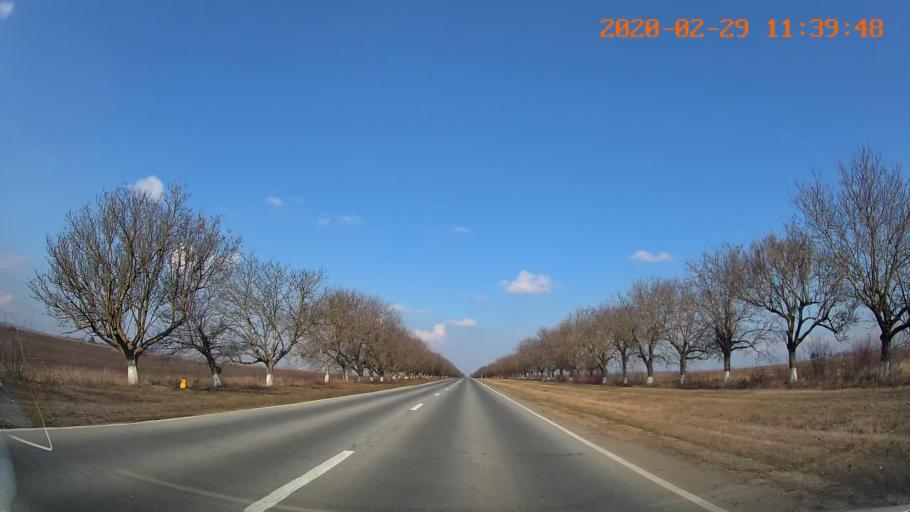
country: MD
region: Rezina
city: Saharna
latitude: 47.6457
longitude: 29.0229
